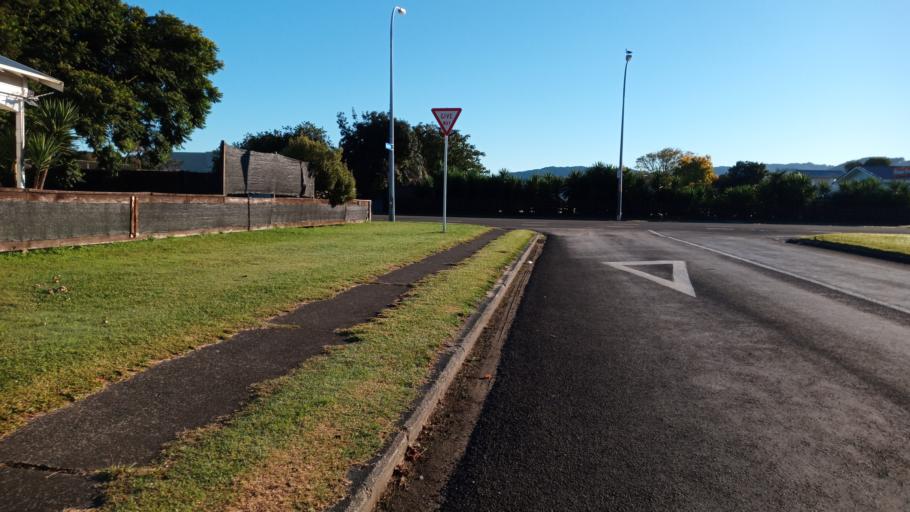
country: NZ
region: Gisborne
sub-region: Gisborne District
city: Gisborne
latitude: -38.6589
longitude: 178.0019
